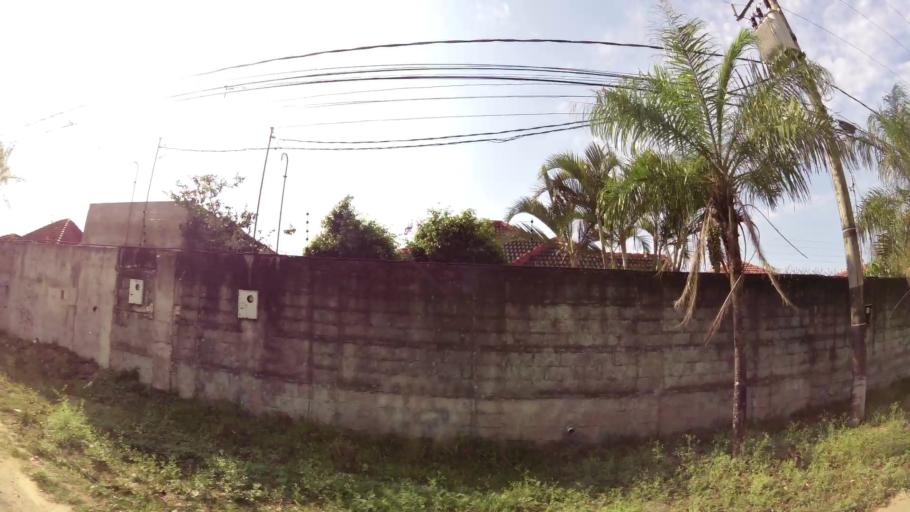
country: BO
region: Santa Cruz
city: Santa Cruz de la Sierra
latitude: -17.7238
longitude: -63.1738
